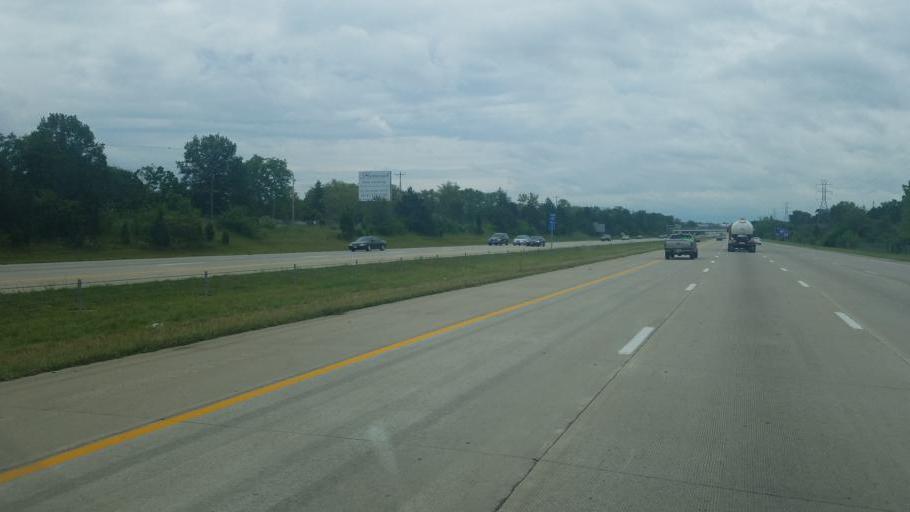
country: US
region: Ohio
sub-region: Franklin County
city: Lincoln Village
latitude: 39.9468
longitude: -83.1205
